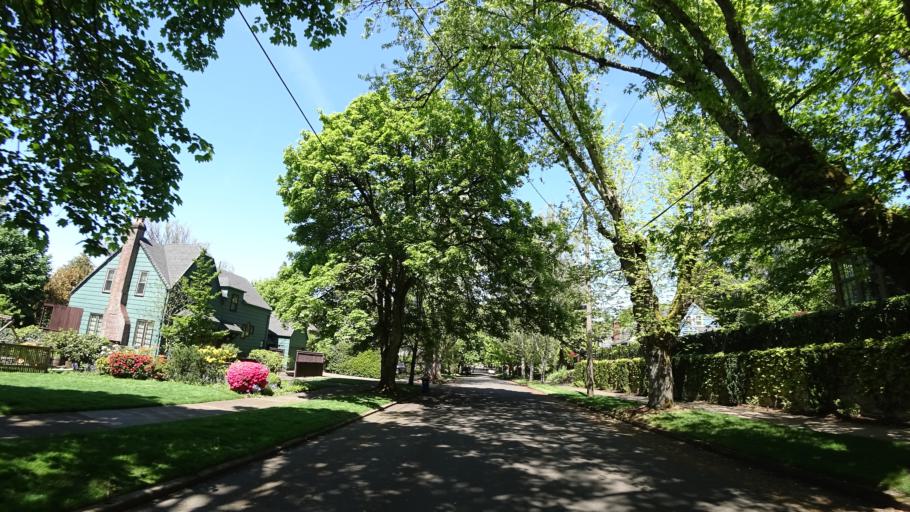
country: US
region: Oregon
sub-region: Clackamas County
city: Milwaukie
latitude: 45.4688
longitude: -122.6345
